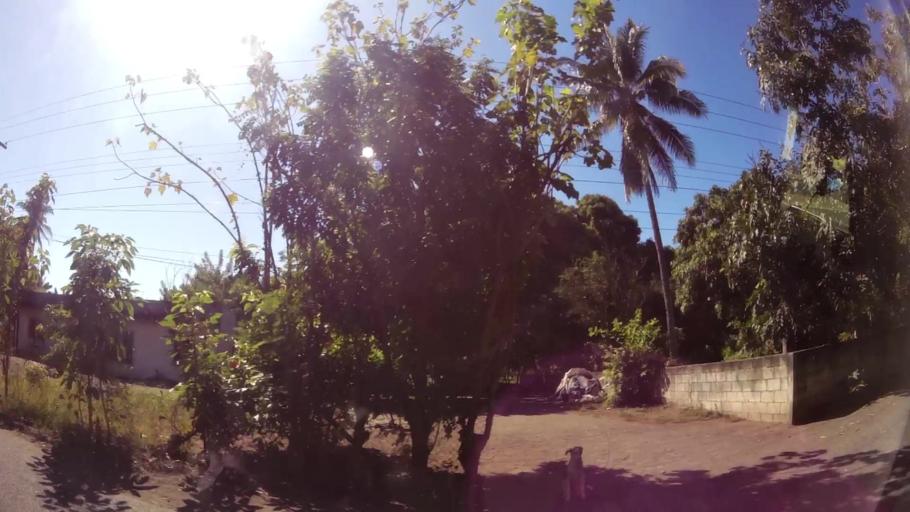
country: GT
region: Escuintla
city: Iztapa
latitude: 13.9247
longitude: -90.5842
